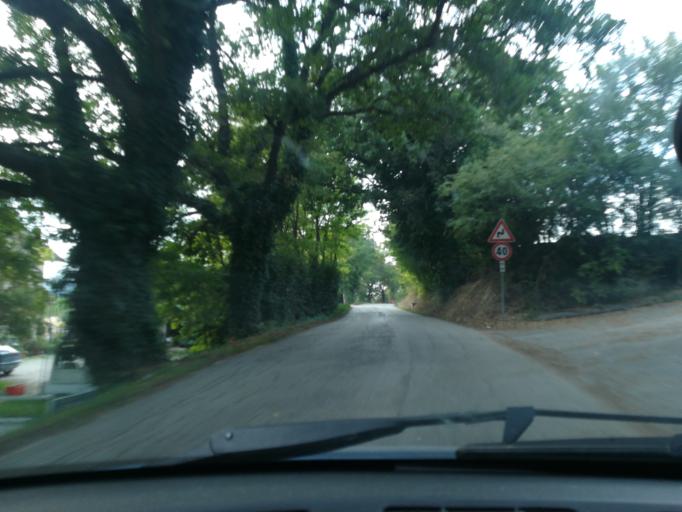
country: IT
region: The Marches
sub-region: Provincia di Macerata
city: Piediripa
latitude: 43.2987
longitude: 13.4809
